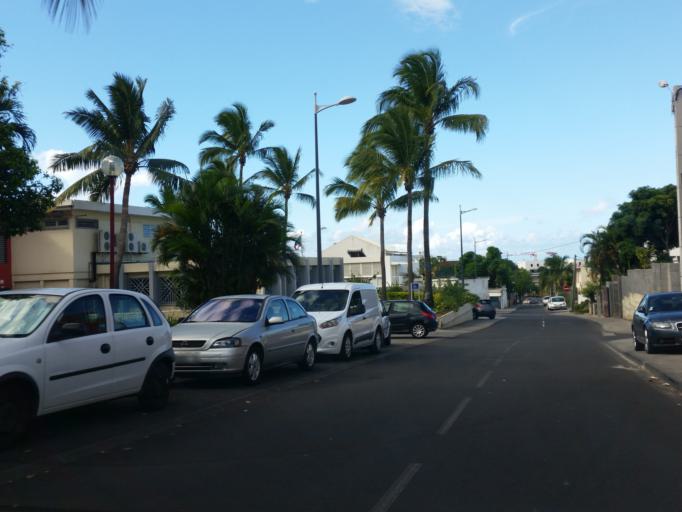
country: RE
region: Reunion
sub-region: Reunion
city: Saint-Denis
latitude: -20.8935
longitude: 55.4794
